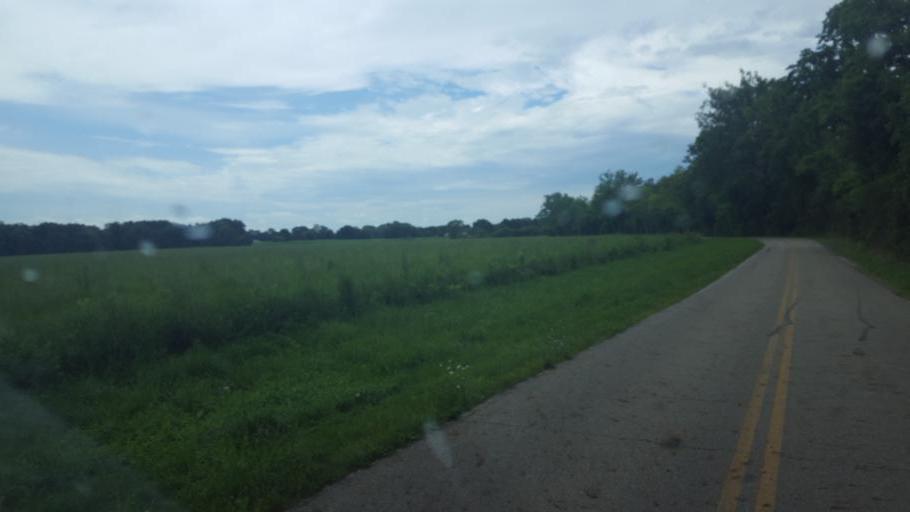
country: US
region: Ohio
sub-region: Pickaway County
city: Ashville
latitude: 39.7059
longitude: -82.9315
